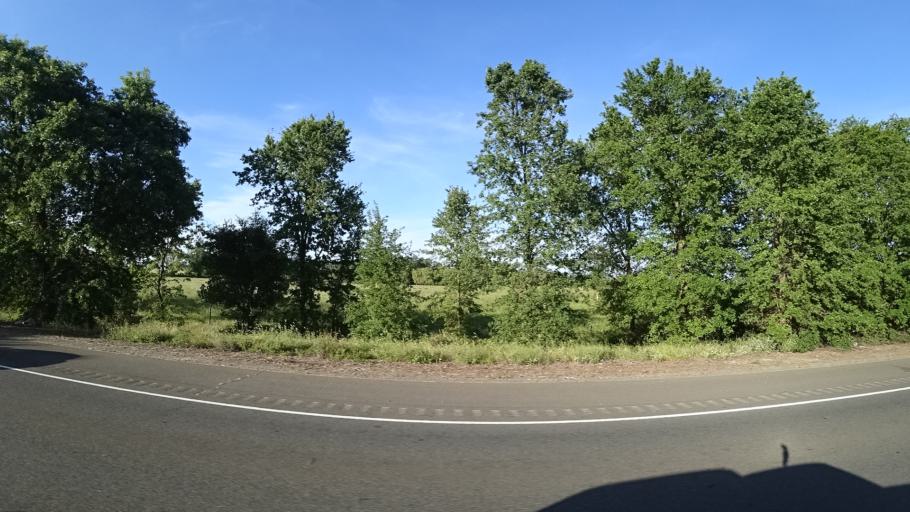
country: US
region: California
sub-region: Placer County
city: Sheridan
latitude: 38.9354
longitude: -121.3481
